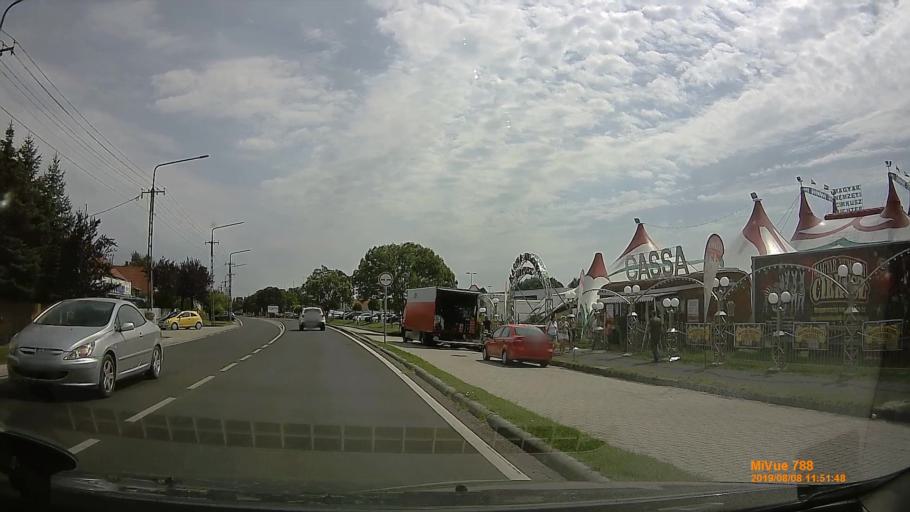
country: HU
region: Somogy
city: Balatonlelle
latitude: 46.7833
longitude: 17.6790
